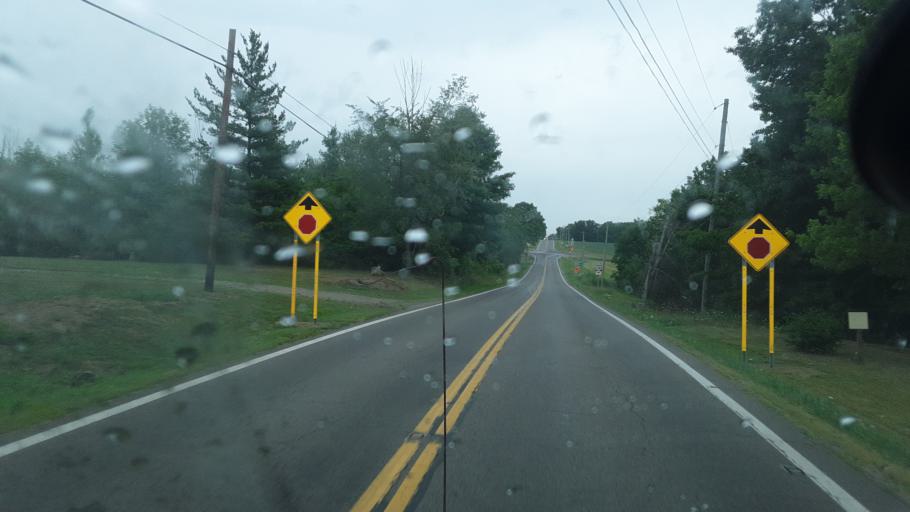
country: US
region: Ohio
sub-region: Williams County
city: Bryan
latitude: 41.4872
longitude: -84.6131
